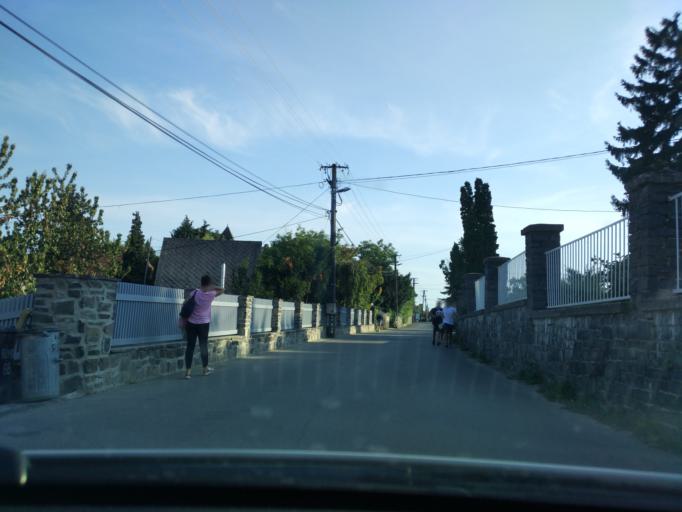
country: HU
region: Veszprem
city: Badacsonytomaj
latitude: 46.8000
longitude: 17.5141
